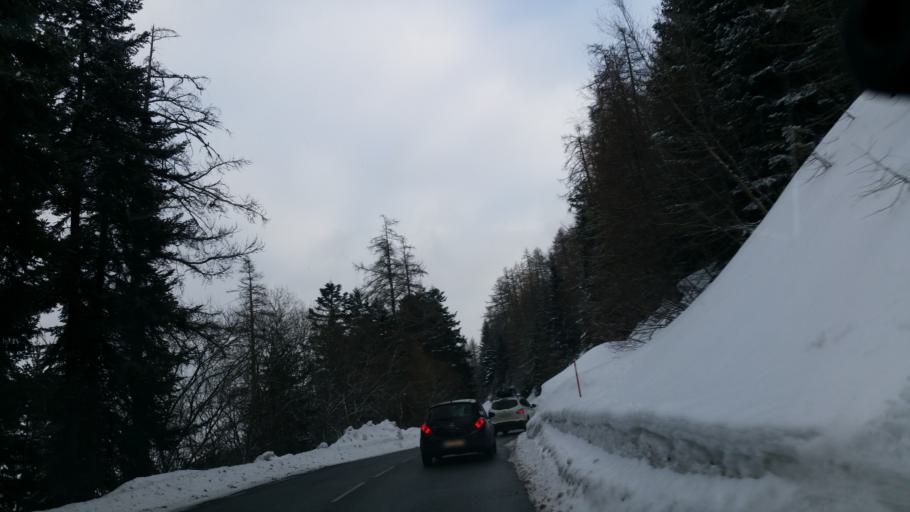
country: FR
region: Rhone-Alpes
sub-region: Departement de la Savoie
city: Villargondran
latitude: 45.2323
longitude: 6.4043
